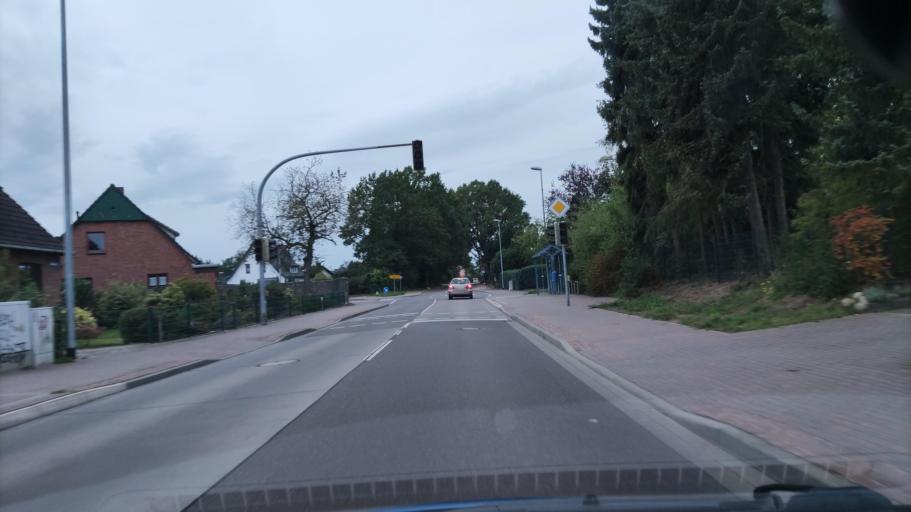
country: DE
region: Schleswig-Holstein
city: Trittau
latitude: 53.6034
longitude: 10.4013
